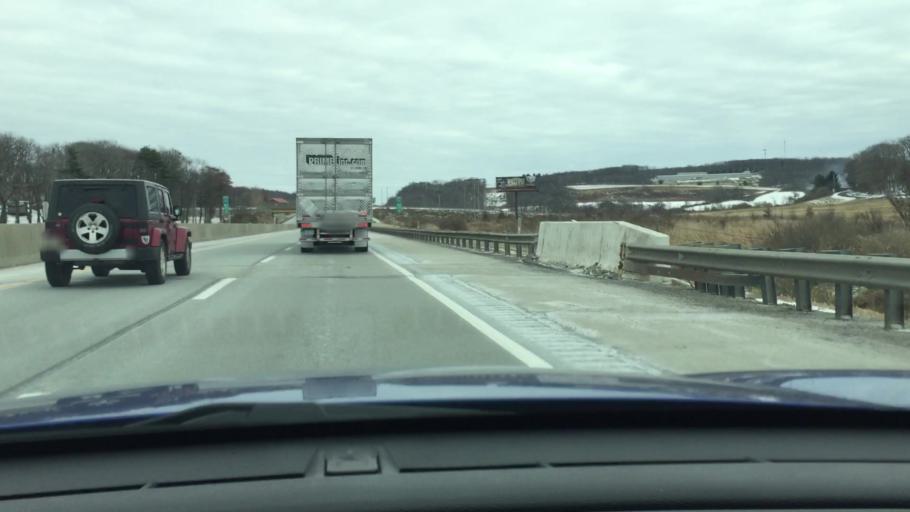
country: US
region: Pennsylvania
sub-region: Somerset County
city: Friedens
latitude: 39.9925
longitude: -78.9973
